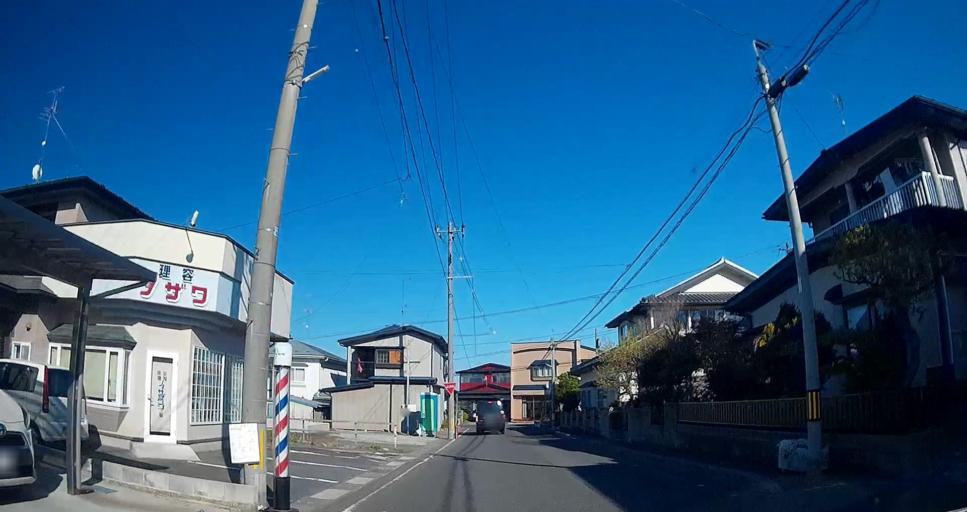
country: JP
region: Aomori
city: Hachinohe
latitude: 40.5254
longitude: 141.5496
